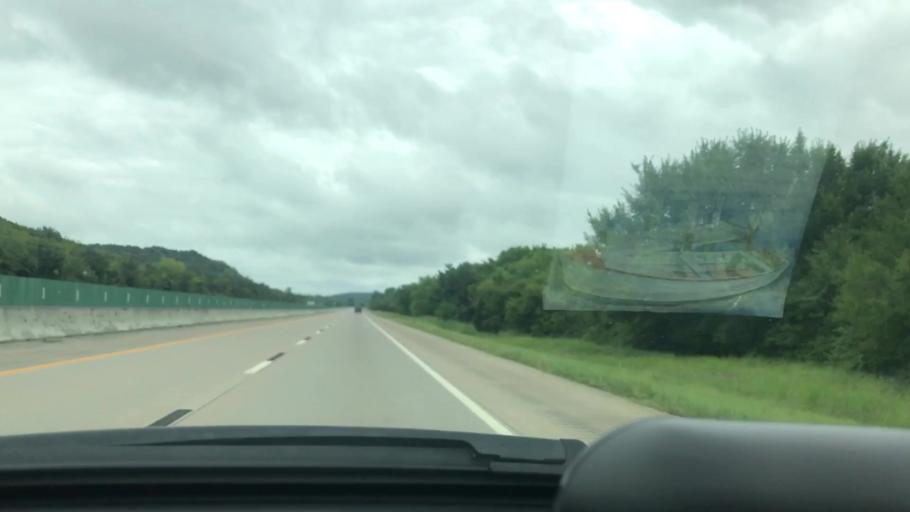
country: US
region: Oklahoma
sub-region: Pittsburg County
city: Krebs
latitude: 35.0850
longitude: -95.7016
